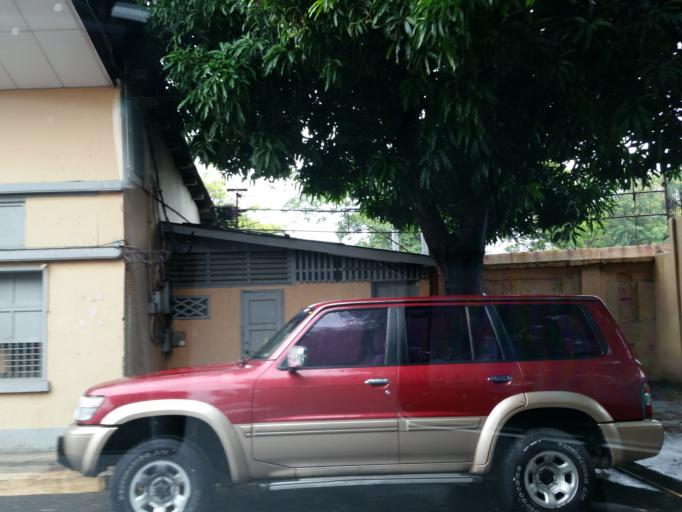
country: NI
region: Managua
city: Managua
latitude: 12.1514
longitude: -86.2830
